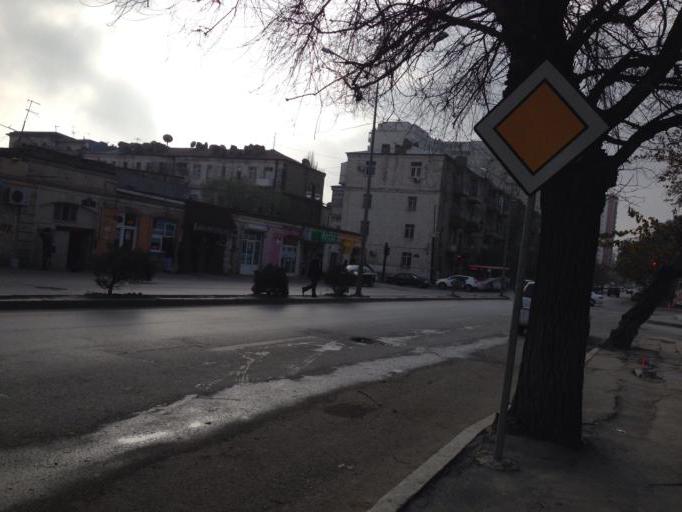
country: AZ
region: Baki
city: Baku
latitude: 40.3926
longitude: 49.8576
